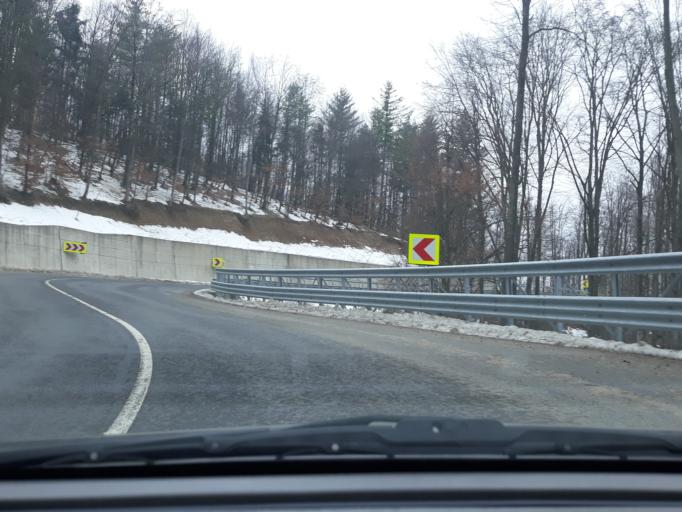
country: RO
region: Bihor
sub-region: Oras Alesd
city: Padurea Neagra
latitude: 47.1289
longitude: 22.4244
